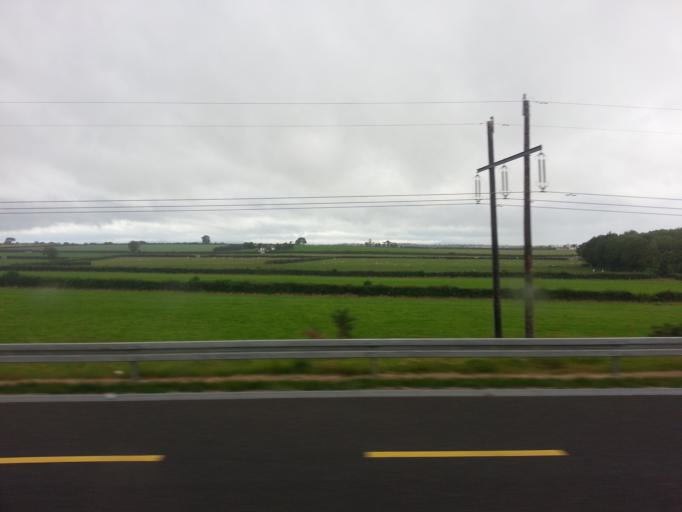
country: IE
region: Leinster
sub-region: Kilkenny
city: Kilkenny
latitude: 52.6379
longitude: -7.1639
